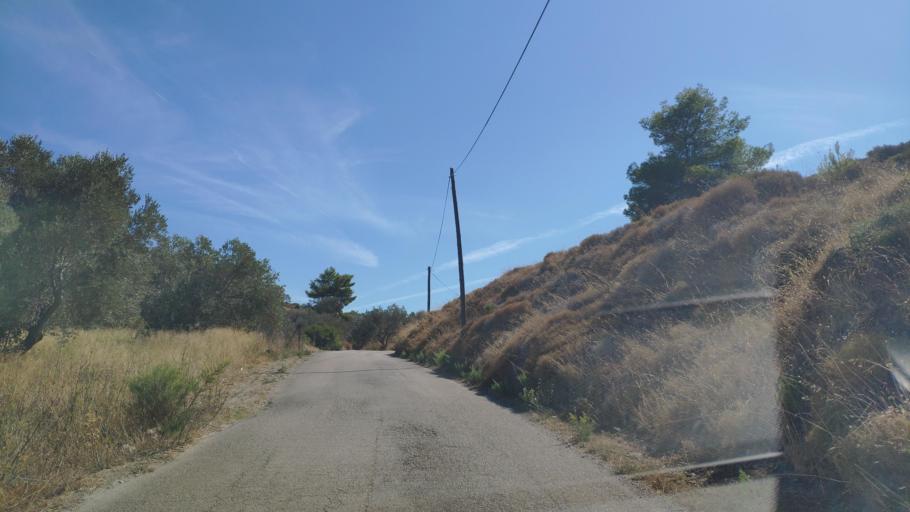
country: GR
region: Attica
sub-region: Nomarchia Anatolikis Attikis
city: Kouvaras
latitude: 37.8337
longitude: 23.9906
